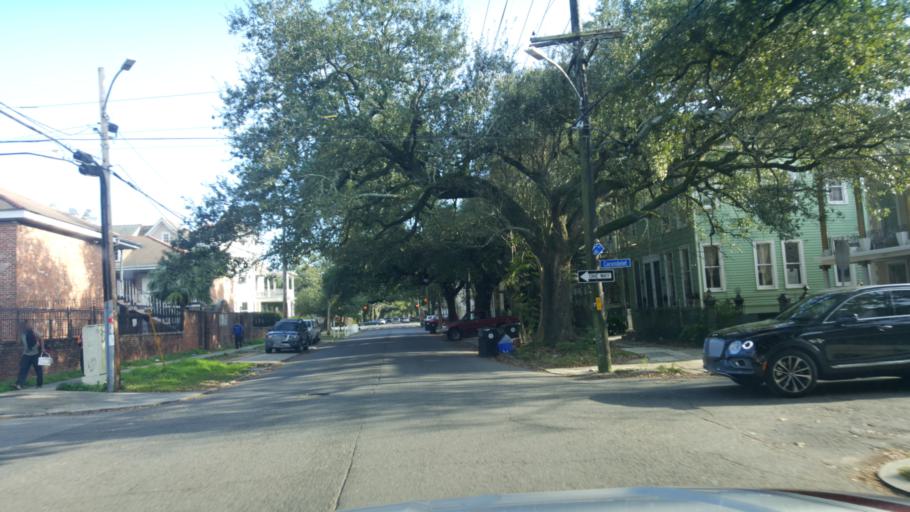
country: US
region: Louisiana
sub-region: Orleans Parish
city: New Orleans
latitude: 29.9320
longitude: -90.0868
